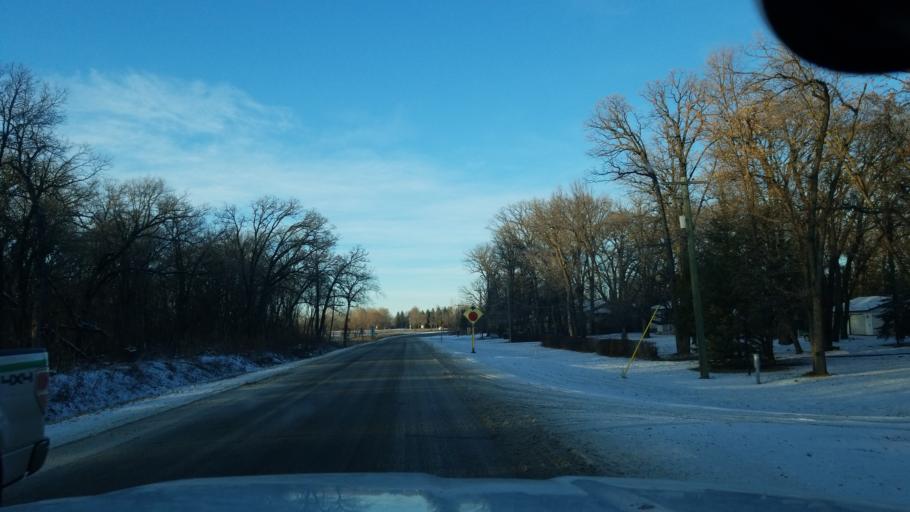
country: CA
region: Manitoba
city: Portage la Prairie
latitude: 49.9519
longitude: -98.3277
